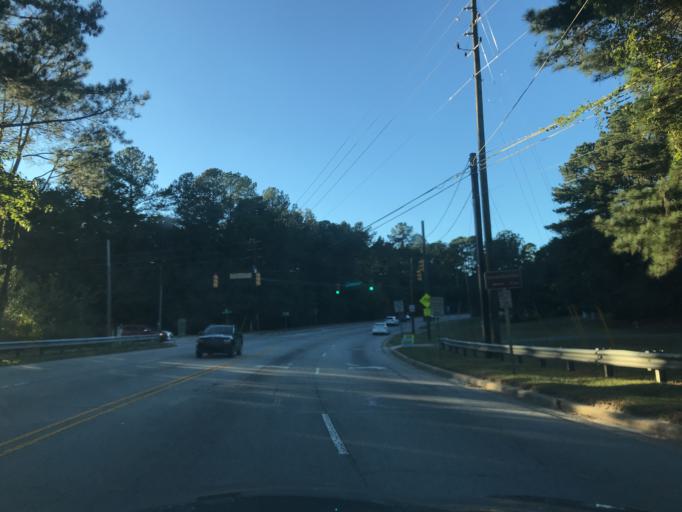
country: US
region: North Carolina
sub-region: Wake County
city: Raleigh
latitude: 35.7503
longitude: -78.6109
